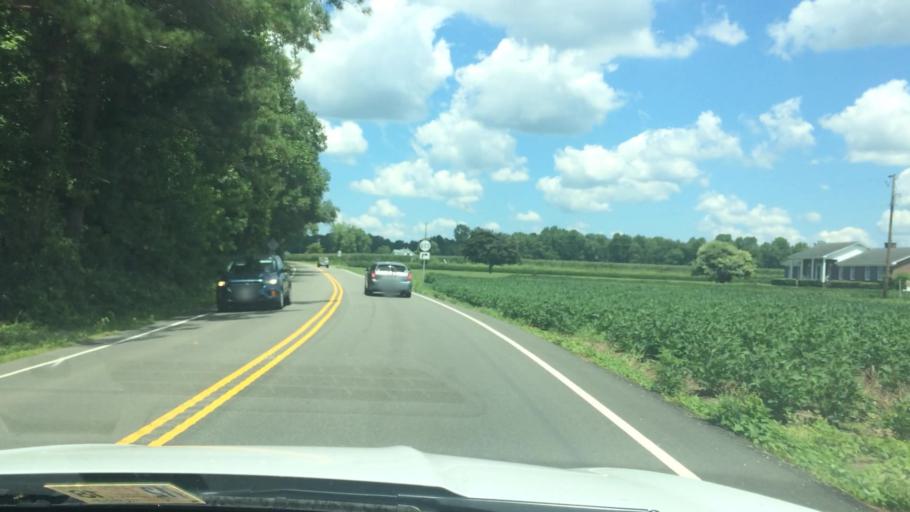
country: US
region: Virginia
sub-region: King William County
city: West Point
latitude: 37.5976
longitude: -76.7648
